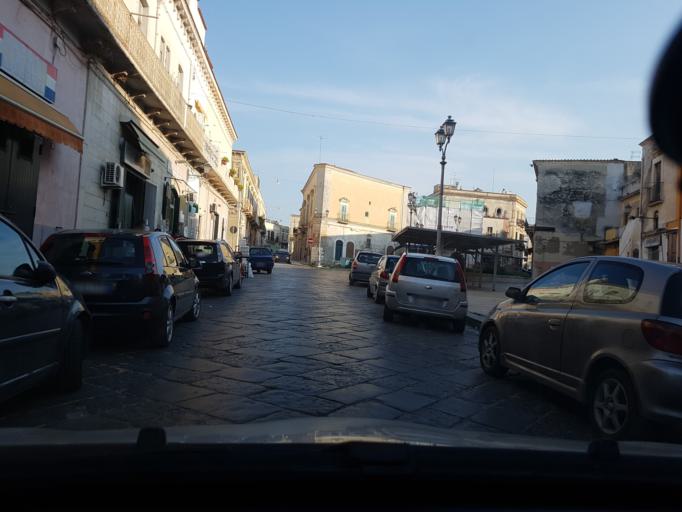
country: IT
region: Apulia
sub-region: Provincia di Foggia
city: Cerignola
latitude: 41.2670
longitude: 15.8948
